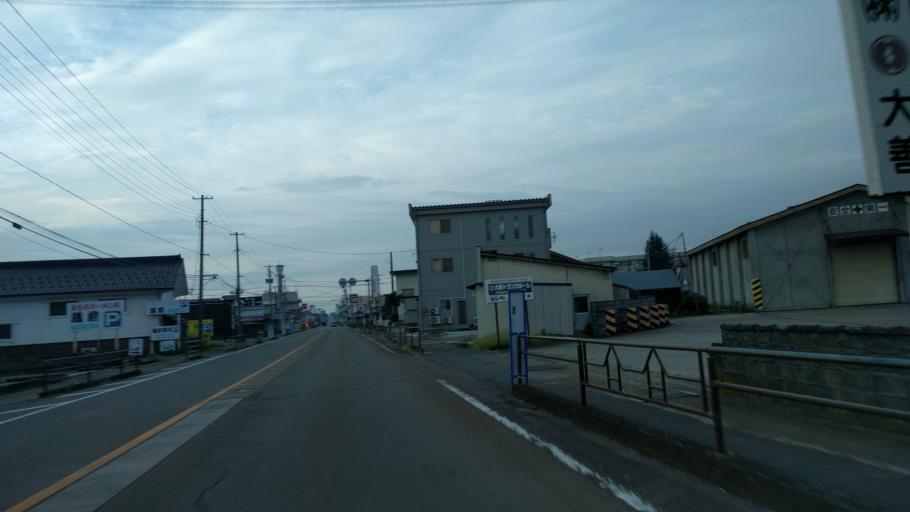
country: JP
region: Fukushima
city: Kitakata
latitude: 37.6526
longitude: 139.8807
